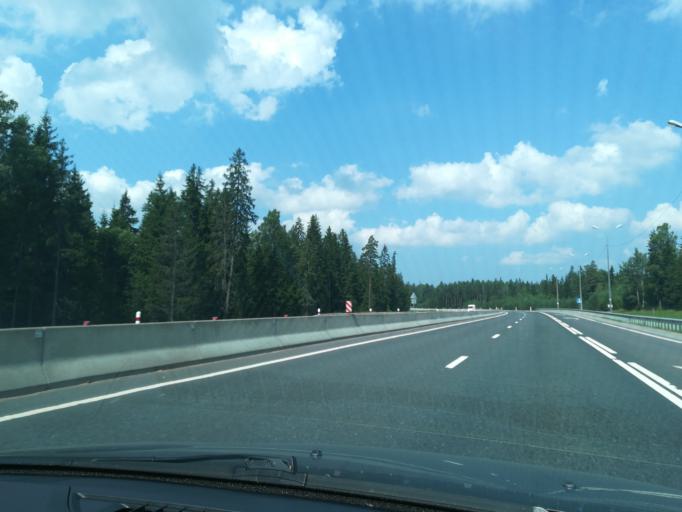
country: RU
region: Leningrad
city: Vistino
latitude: 59.6420
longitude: 28.5704
